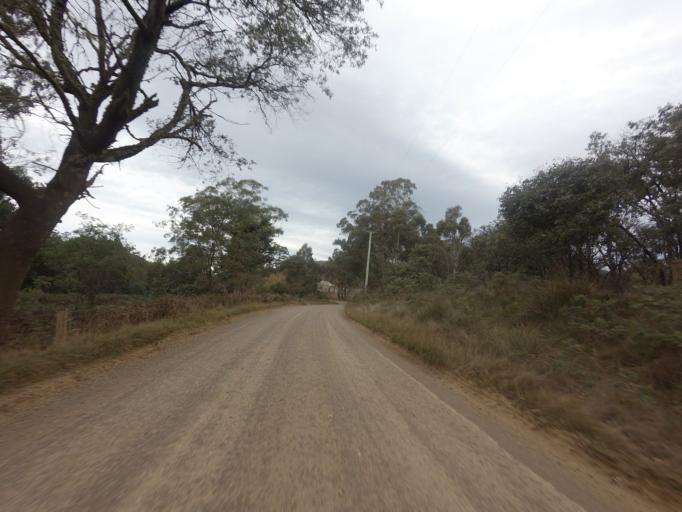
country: AU
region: Tasmania
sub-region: Derwent Valley
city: New Norfolk
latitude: -42.5775
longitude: 147.0024
